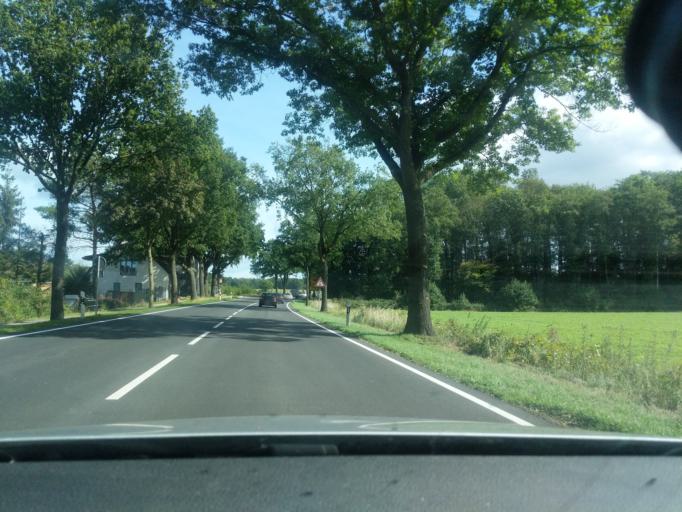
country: DE
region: Lower Saxony
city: Ostercappeln
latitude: 52.3342
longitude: 8.1800
